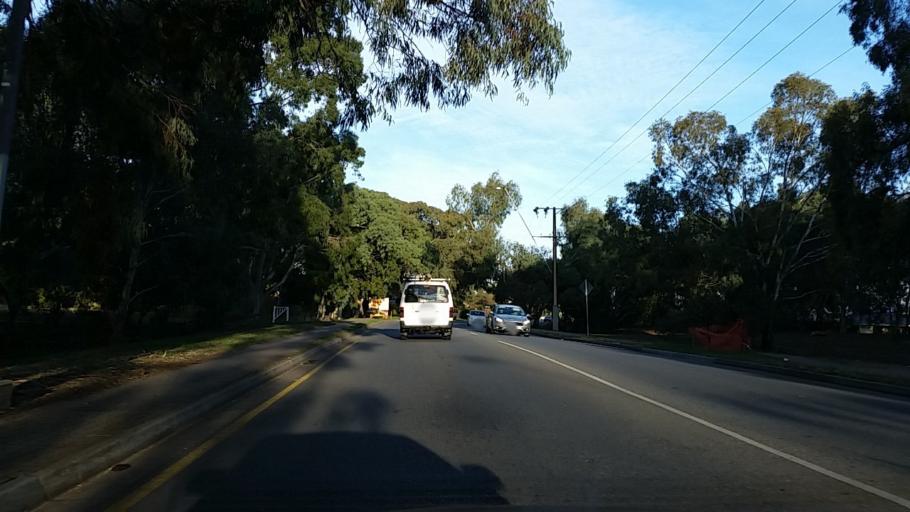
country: AU
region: South Australia
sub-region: Salisbury
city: Salisbury
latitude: -34.7623
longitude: 138.6201
